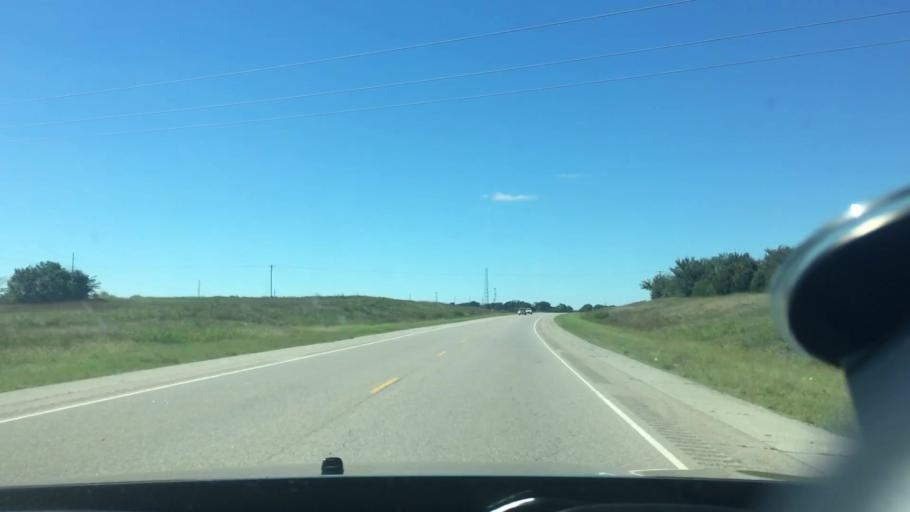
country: US
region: Oklahoma
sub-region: Coal County
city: Coalgate
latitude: 34.6130
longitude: -96.4386
